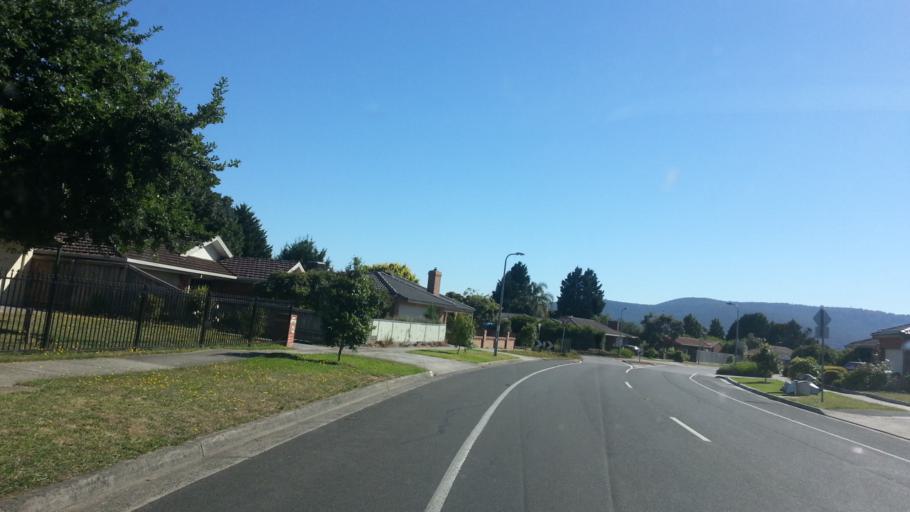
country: AU
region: Victoria
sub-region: Knox
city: Knoxfield
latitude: -37.9157
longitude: 145.2575
